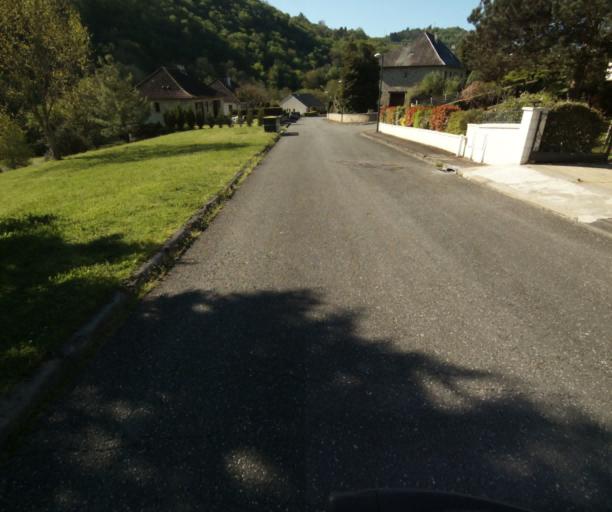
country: FR
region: Limousin
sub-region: Departement de la Correze
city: Tulle
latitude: 45.2830
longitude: 1.7862
